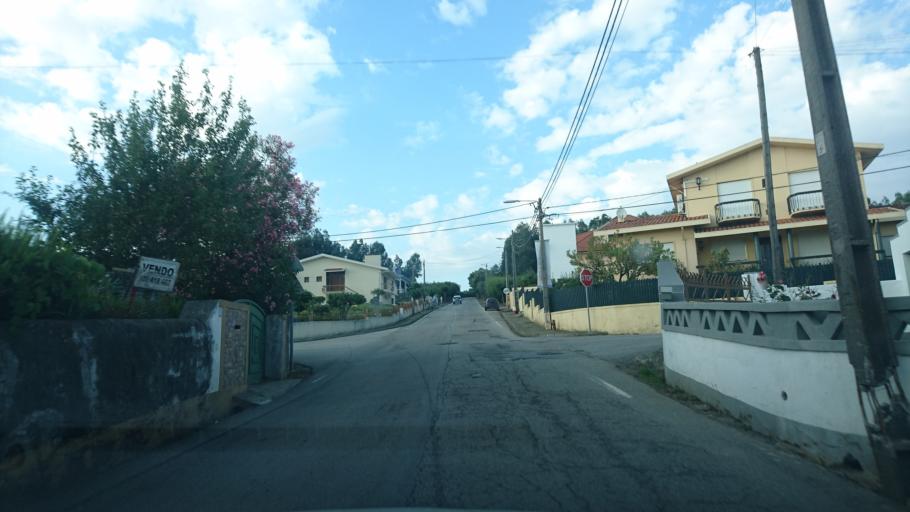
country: PT
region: Aveiro
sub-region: Santa Maria da Feira
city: Sao Joao de Ver
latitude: 40.9560
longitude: -8.5503
